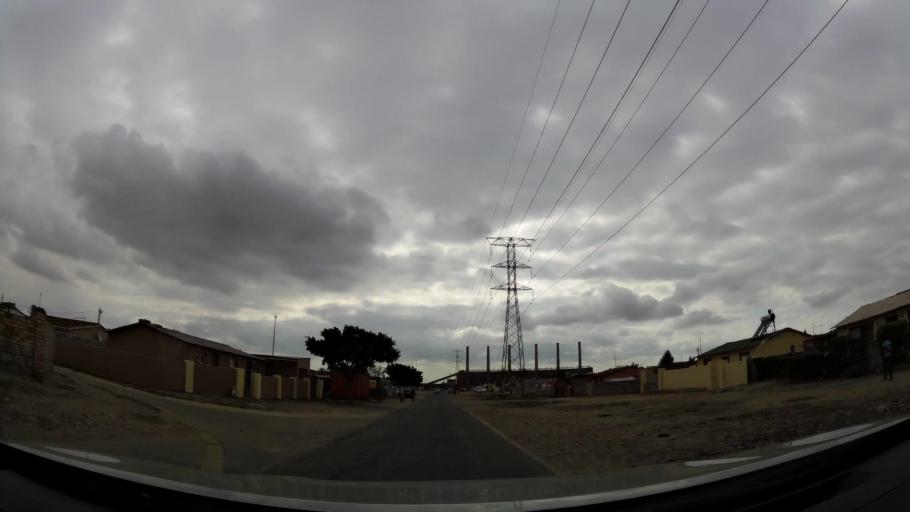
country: ZA
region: Eastern Cape
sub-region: Nelson Mandela Bay Metropolitan Municipality
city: Port Elizabeth
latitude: -33.8781
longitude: 25.5965
